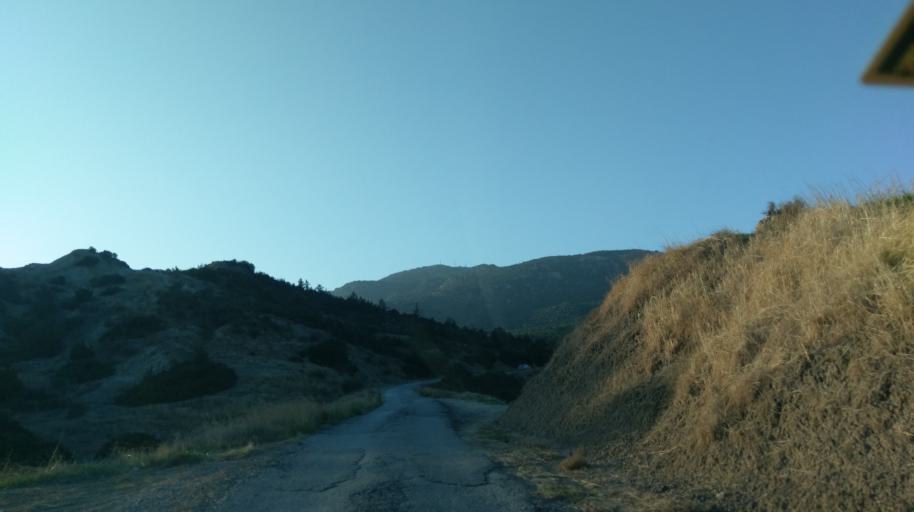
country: CY
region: Ammochostos
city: Trikomo
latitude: 35.3676
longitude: 33.9092
